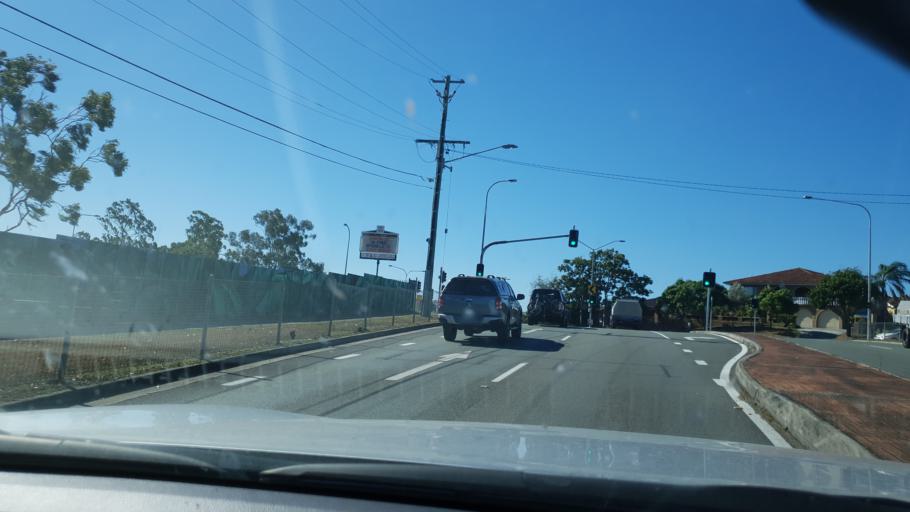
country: AU
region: Queensland
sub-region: Brisbane
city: Everton Park
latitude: -27.3982
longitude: 152.9867
